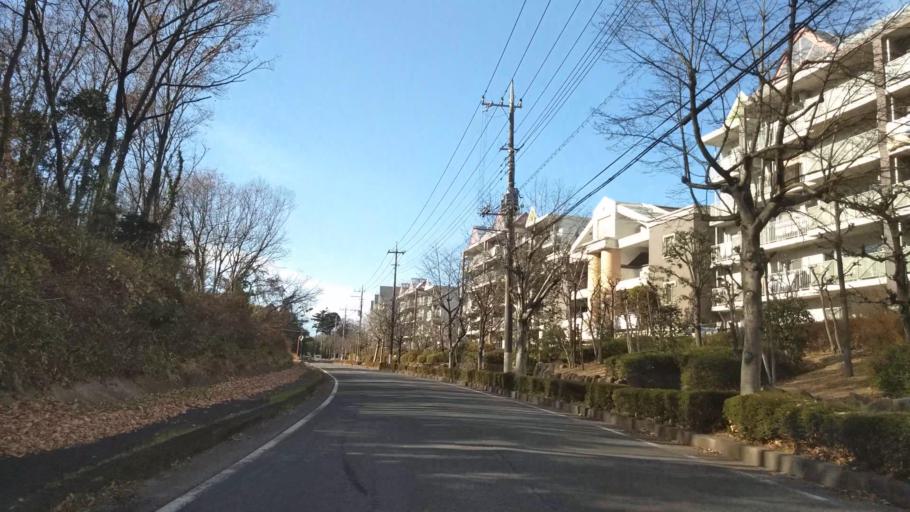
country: JP
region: Kanagawa
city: Hadano
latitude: 35.3525
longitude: 139.2295
